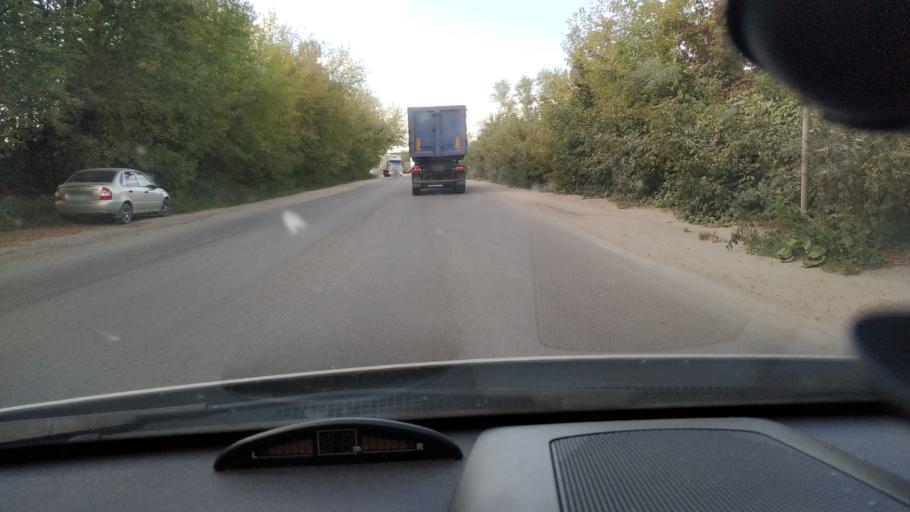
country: RU
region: Rjazan
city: Ryazan'
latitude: 54.6631
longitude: 39.6284
